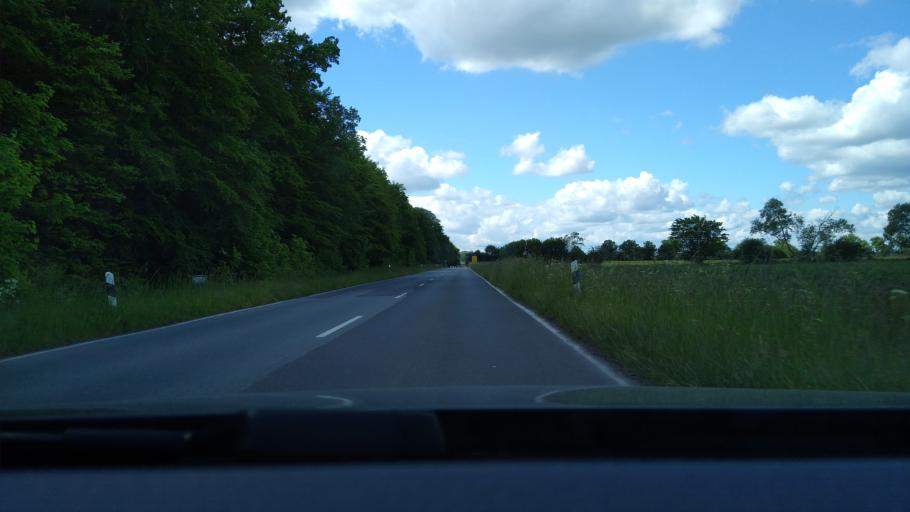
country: DE
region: Schleswig-Holstein
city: Kellenhusen
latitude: 54.2093
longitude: 11.0448
